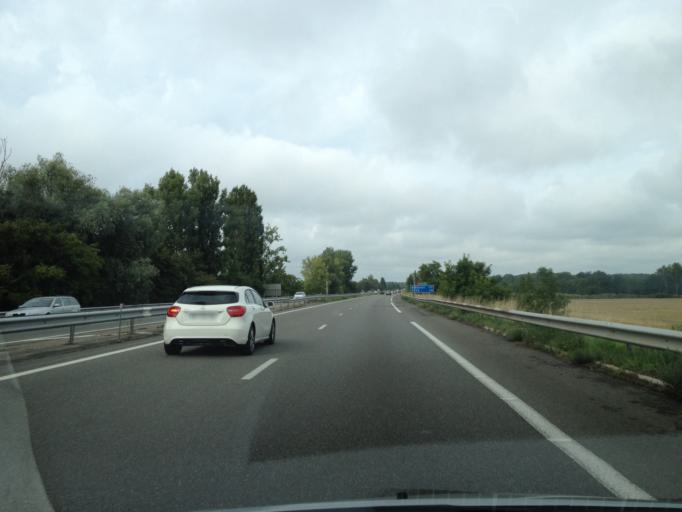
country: FR
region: Midi-Pyrenees
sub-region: Departement du Tarn-et-Garonne
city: Castelsarrasin
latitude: 44.0479
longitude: 1.0822
